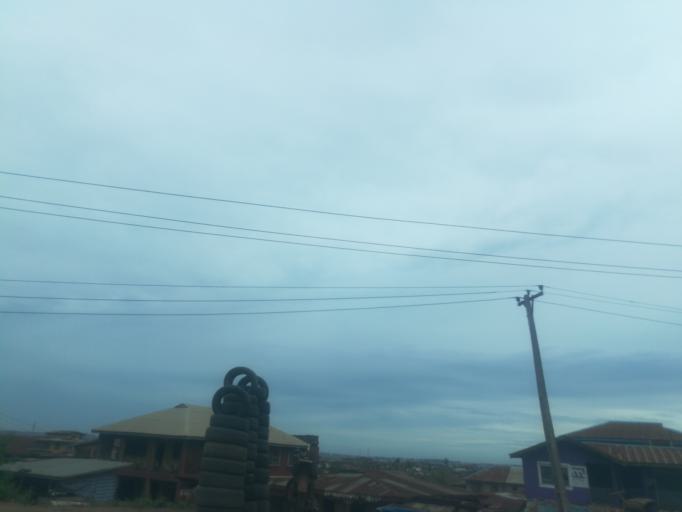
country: NG
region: Oyo
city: Ibadan
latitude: 7.3459
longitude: 3.9188
